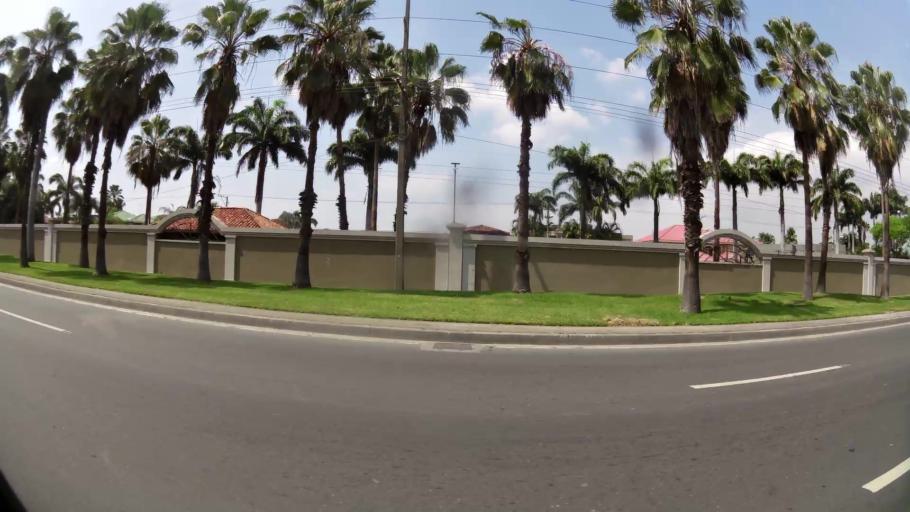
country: EC
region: Guayas
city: Eloy Alfaro
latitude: -2.1361
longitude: -79.8632
